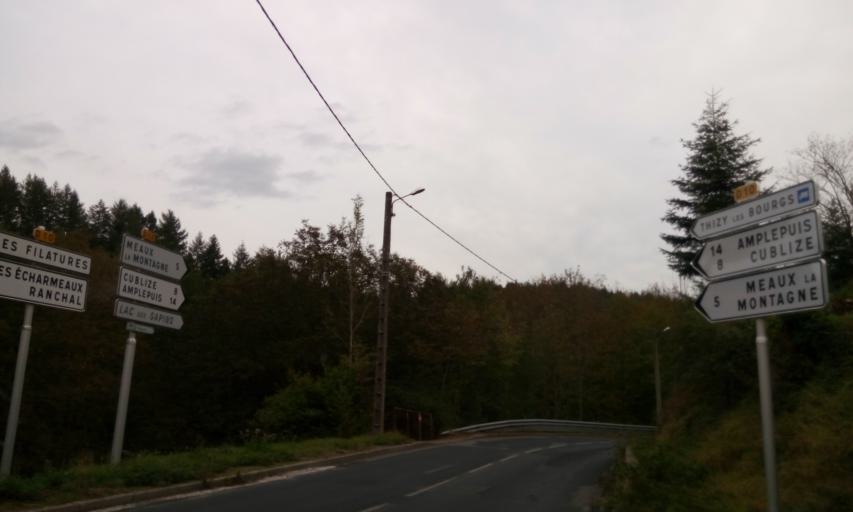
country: FR
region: Rhone-Alpes
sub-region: Departement du Rhone
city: Cublize
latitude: 46.0727
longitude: 4.3920
